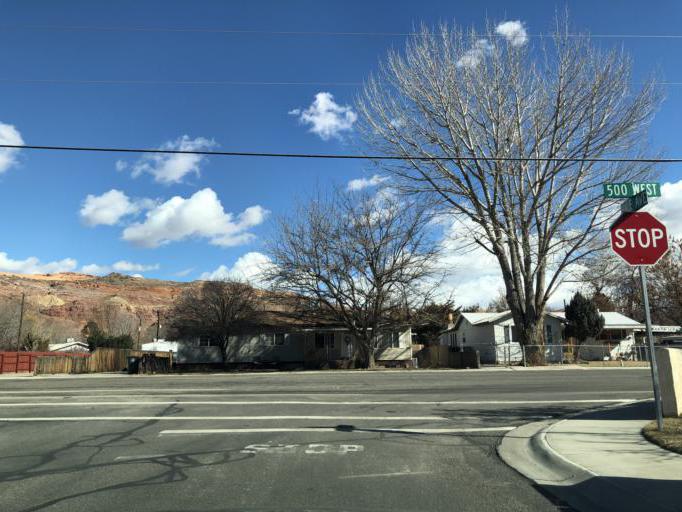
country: US
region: Utah
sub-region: Grand County
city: Moab
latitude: 38.5807
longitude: -109.5615
